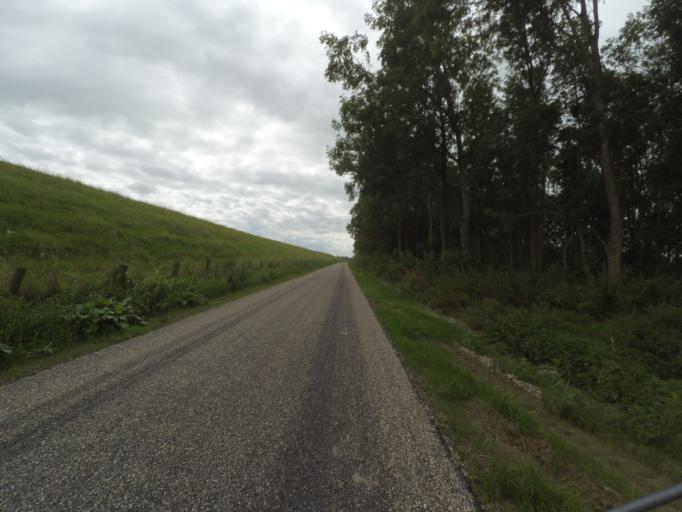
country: NL
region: Friesland
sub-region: Gemeente Dongeradeel
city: Anjum
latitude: 53.3566
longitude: 6.1460
